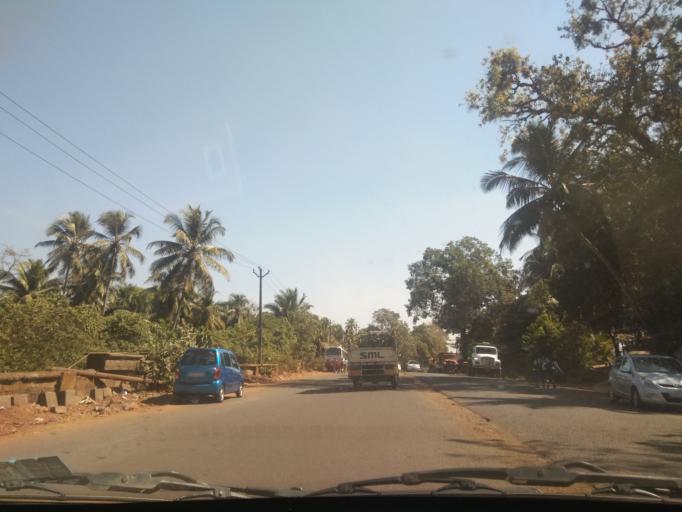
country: IN
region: Goa
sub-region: North Goa
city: Dicholi
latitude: 15.5900
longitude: 73.9489
